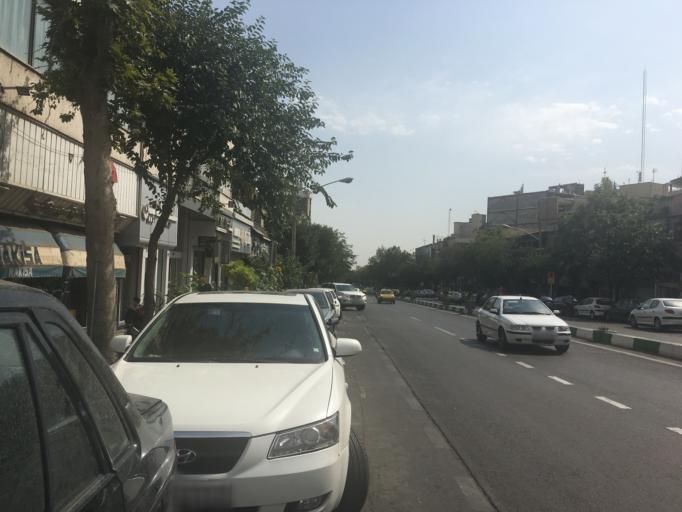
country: IR
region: Tehran
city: Tehran
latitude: 35.7352
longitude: 51.4415
